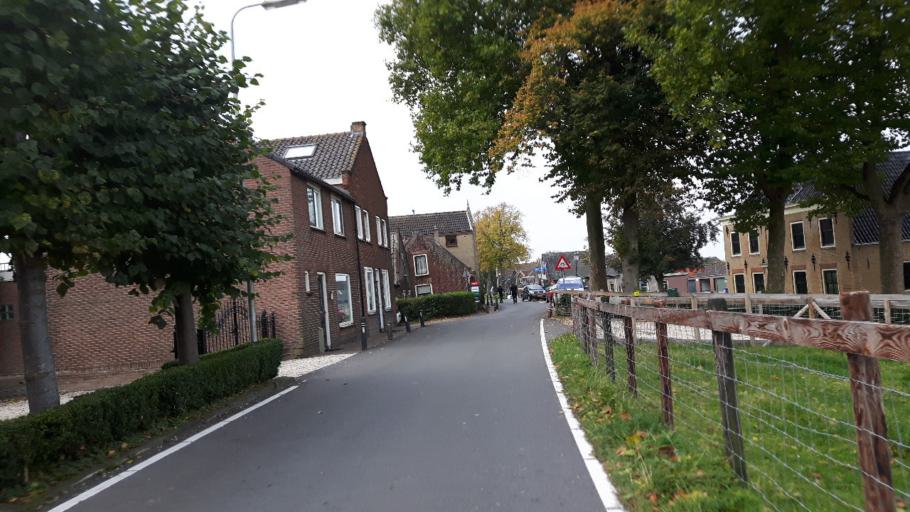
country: NL
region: South Holland
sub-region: Gemeente Vlist
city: Vlist
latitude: 52.0145
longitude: 4.8120
